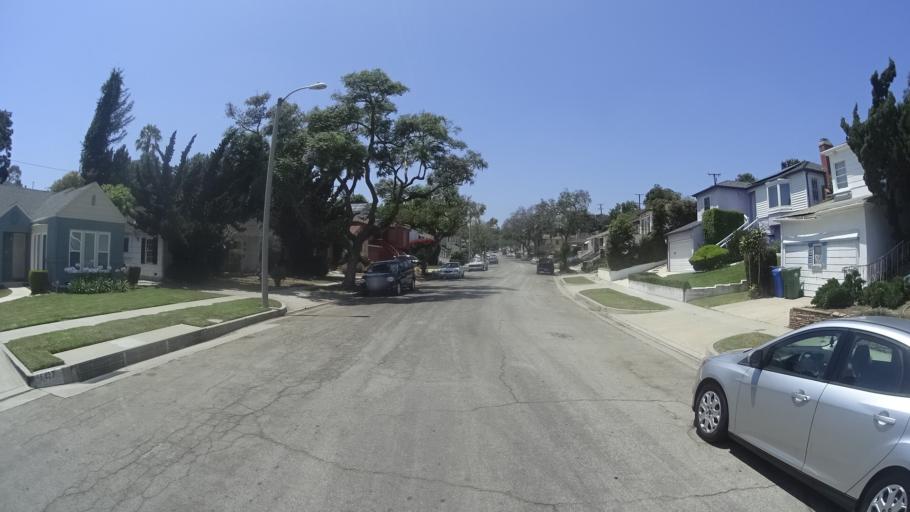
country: US
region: California
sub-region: Los Angeles County
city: View Park-Windsor Hills
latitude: 33.9923
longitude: -118.3494
